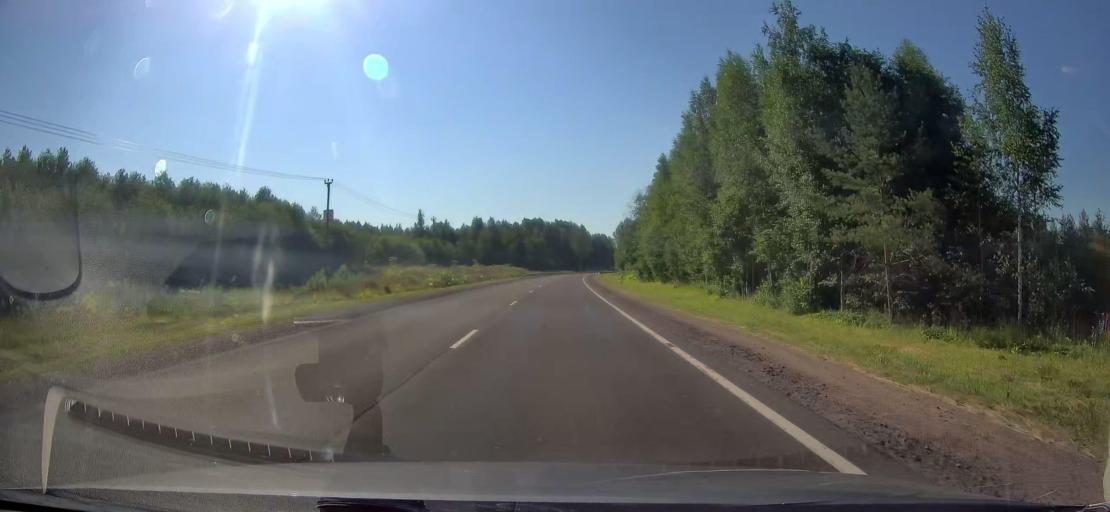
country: RU
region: Leningrad
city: Khvalovo
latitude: 59.8745
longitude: 32.8709
